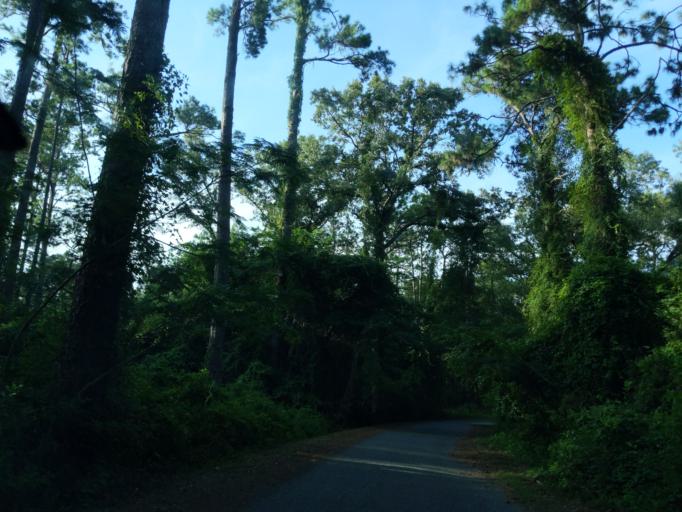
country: US
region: Florida
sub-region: Leon County
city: Tallahassee
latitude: 30.3502
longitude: -84.3635
